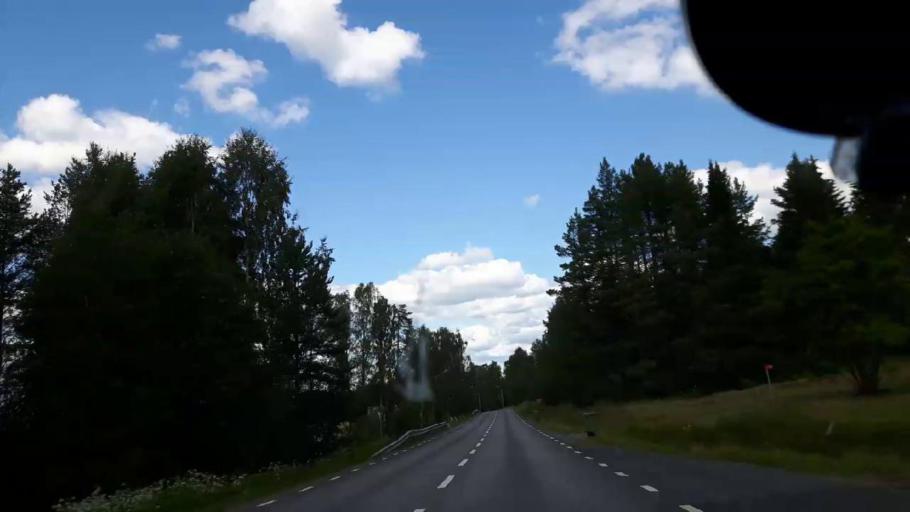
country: SE
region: Jaemtland
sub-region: Ragunda Kommun
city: Hammarstrand
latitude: 63.0006
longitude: 16.6759
